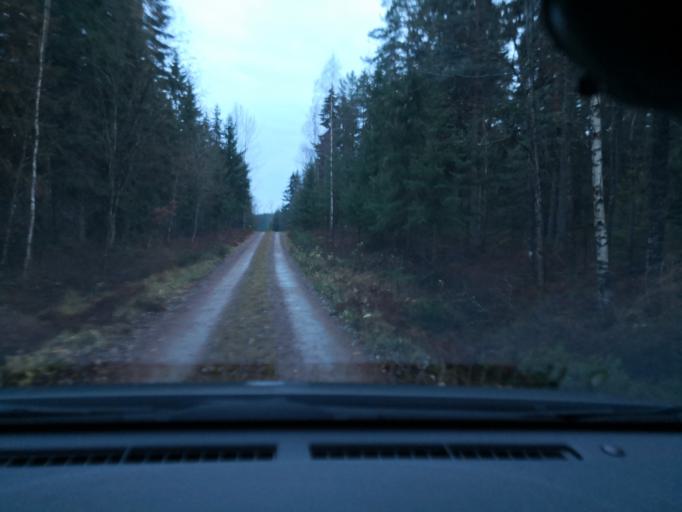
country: SE
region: Vaestmanland
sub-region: Hallstahammars Kommun
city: Kolback
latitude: 59.5477
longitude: 16.1708
